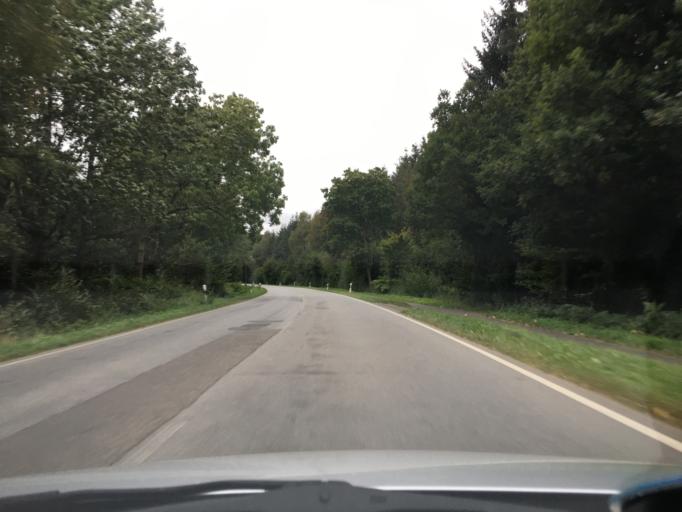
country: DE
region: Schleswig-Holstein
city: Neudorf-Bornstein
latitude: 54.4484
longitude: 9.9214
